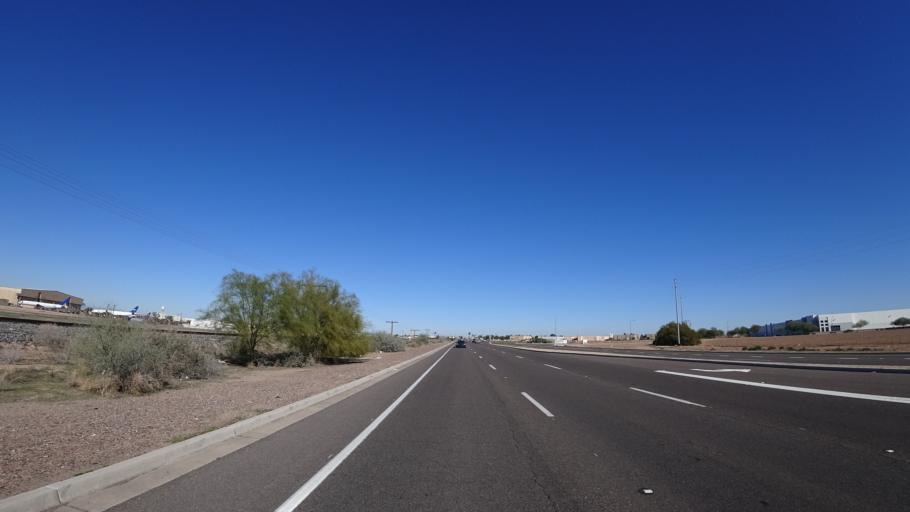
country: US
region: Arizona
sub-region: Maricopa County
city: Goodyear
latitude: 33.4209
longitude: -112.3648
